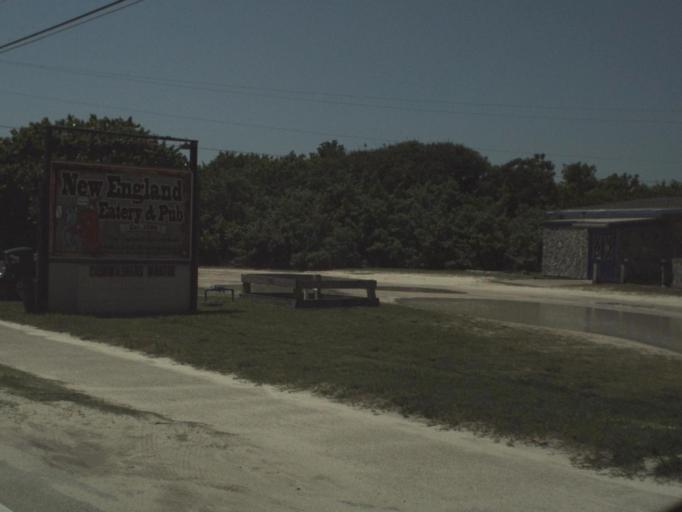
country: US
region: Florida
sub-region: Brevard County
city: Malabar
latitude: 27.9693
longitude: -80.5097
